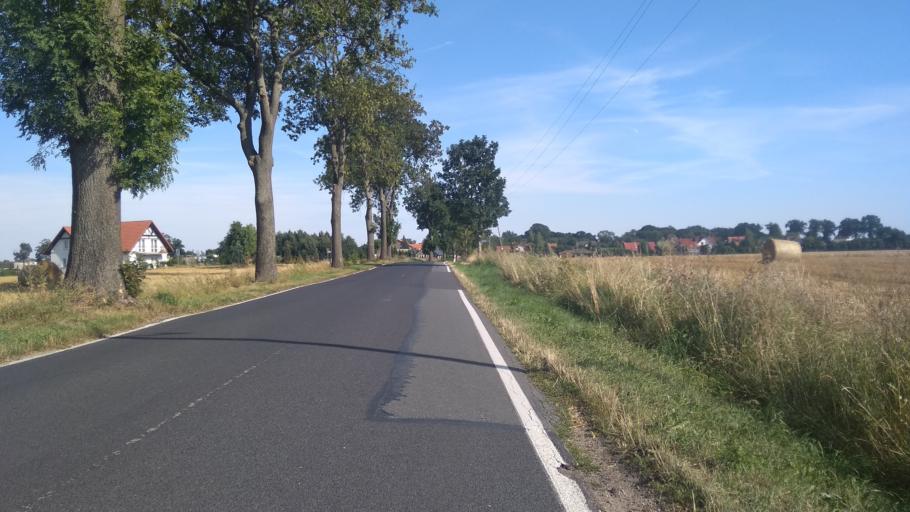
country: PL
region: Kujawsko-Pomorskie
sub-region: Bydgoszcz
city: Fordon
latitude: 53.2138
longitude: 18.1508
